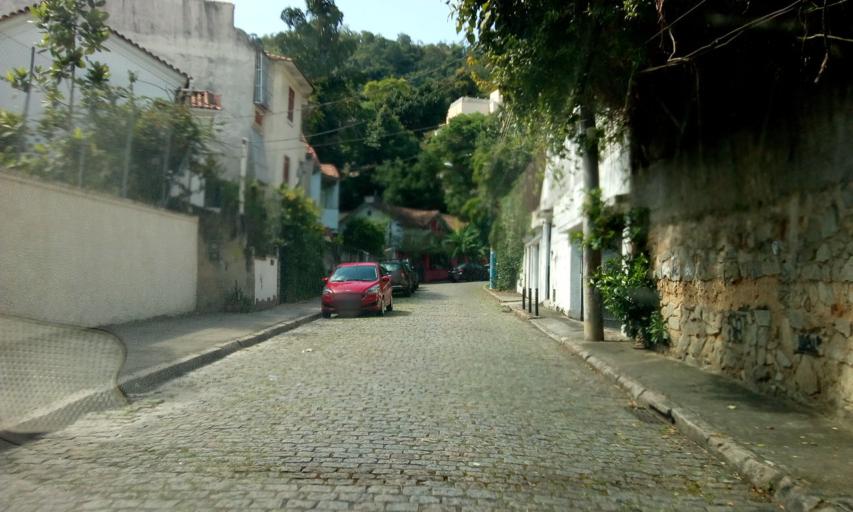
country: BR
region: Rio de Janeiro
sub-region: Rio De Janeiro
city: Rio de Janeiro
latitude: -22.9220
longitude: -43.1899
